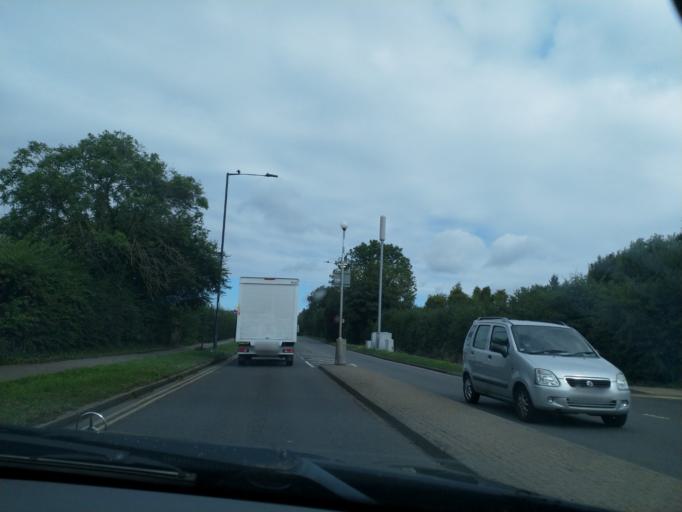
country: GB
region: England
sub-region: Greater London
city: Harrow on the Hill
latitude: 51.5711
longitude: -0.3233
